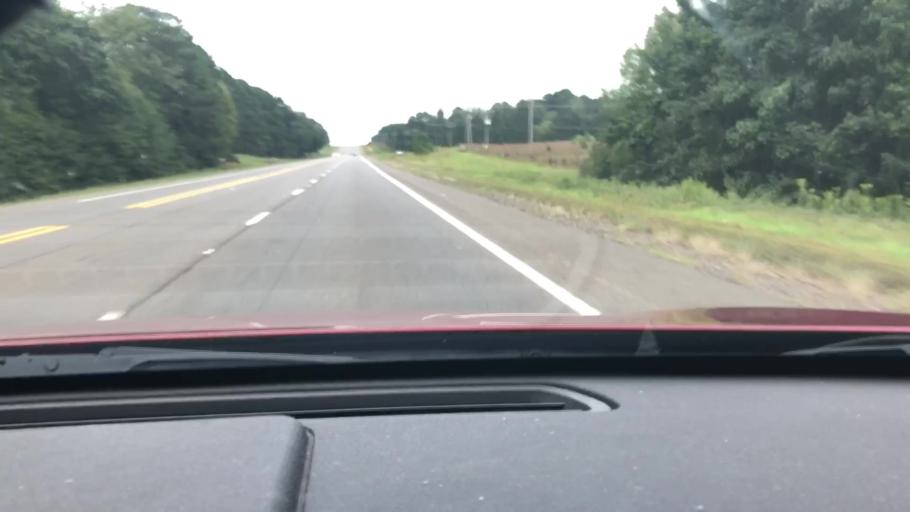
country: US
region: Arkansas
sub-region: Lafayette County
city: Stamps
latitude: 33.3631
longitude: -93.4657
